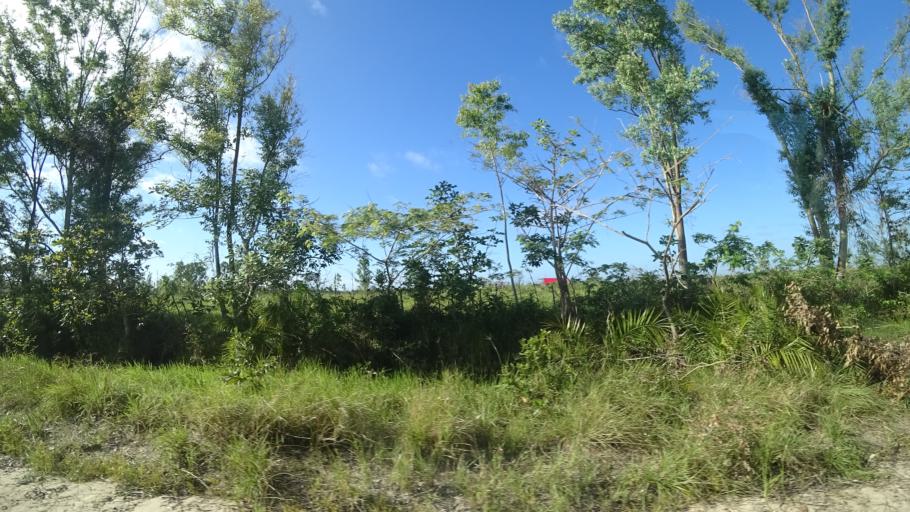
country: MZ
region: Sofala
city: Beira
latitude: -19.7258
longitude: 34.9910
